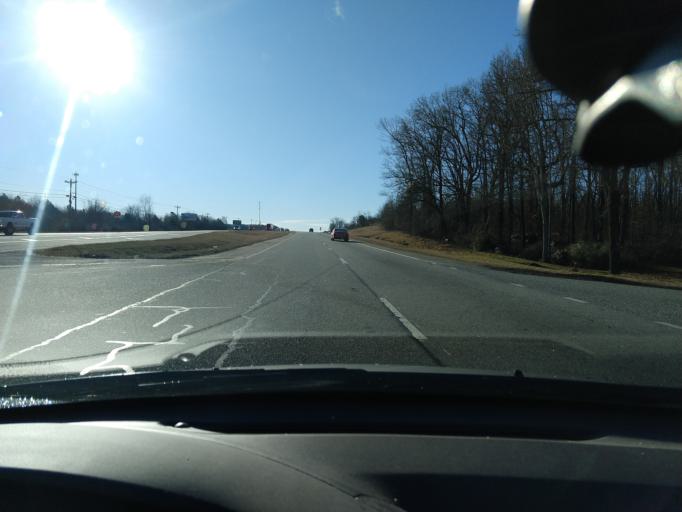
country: US
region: Georgia
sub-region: Jackson County
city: Commerce
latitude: 34.2407
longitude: -83.4567
